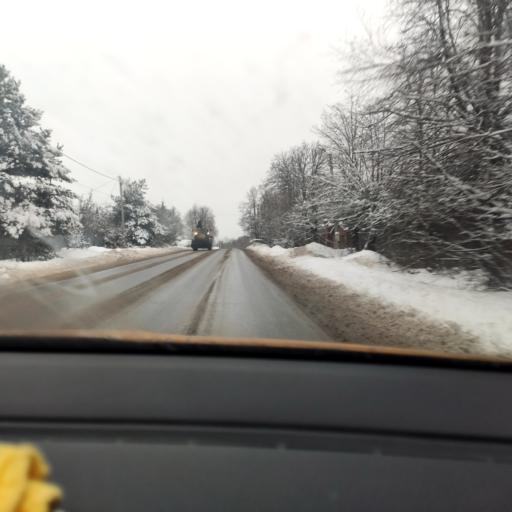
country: RU
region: Moskovskaya
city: Zvenigorod
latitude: 55.7500
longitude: 36.8760
